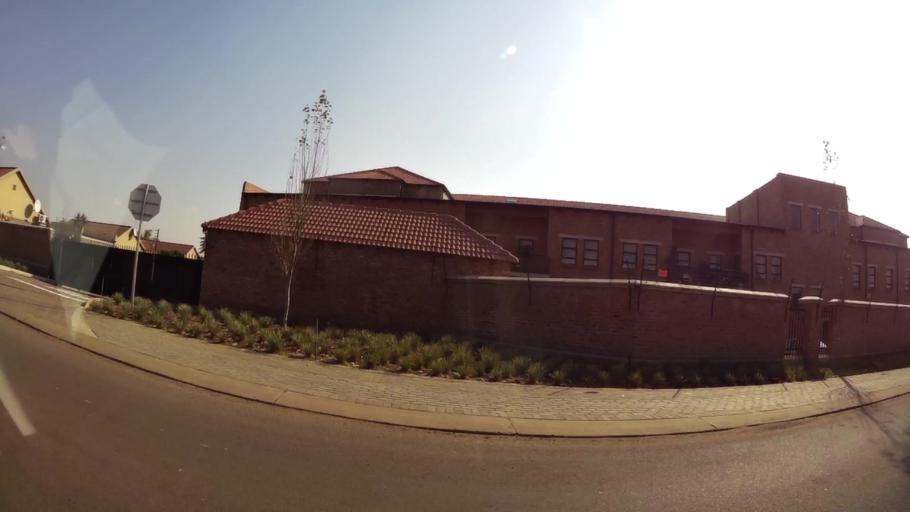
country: ZA
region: Gauteng
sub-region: City of Tshwane Metropolitan Municipality
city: Pretoria
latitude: -25.7725
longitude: 28.3482
